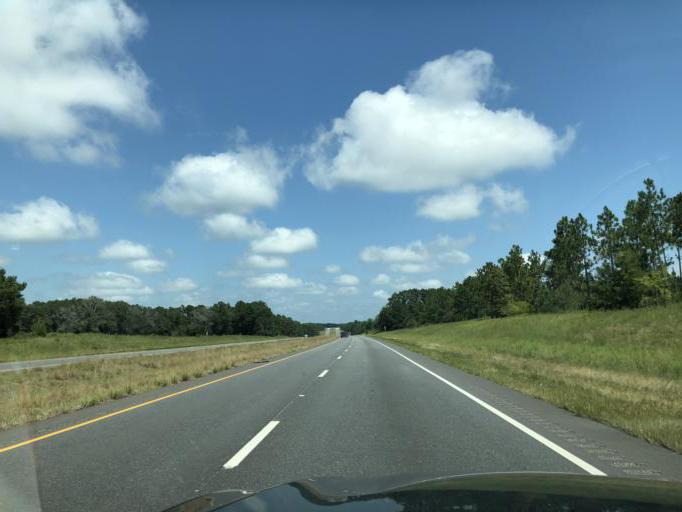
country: US
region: Alabama
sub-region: Henry County
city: Abbeville
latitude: 31.5114
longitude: -85.2909
